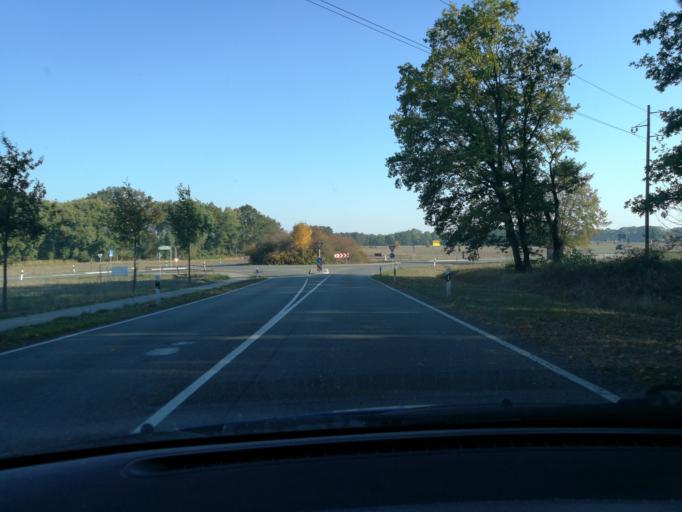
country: DE
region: Lower Saxony
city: Dannenberg
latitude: 53.1013
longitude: 11.0573
